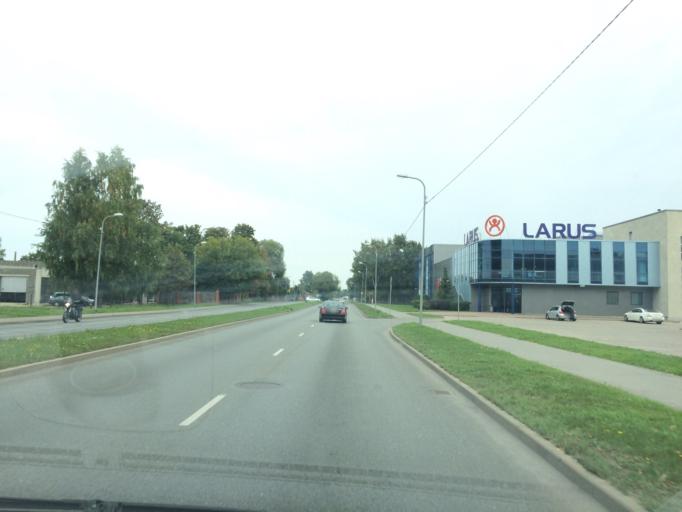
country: LV
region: Riga
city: Riga
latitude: 56.9422
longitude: 24.1821
